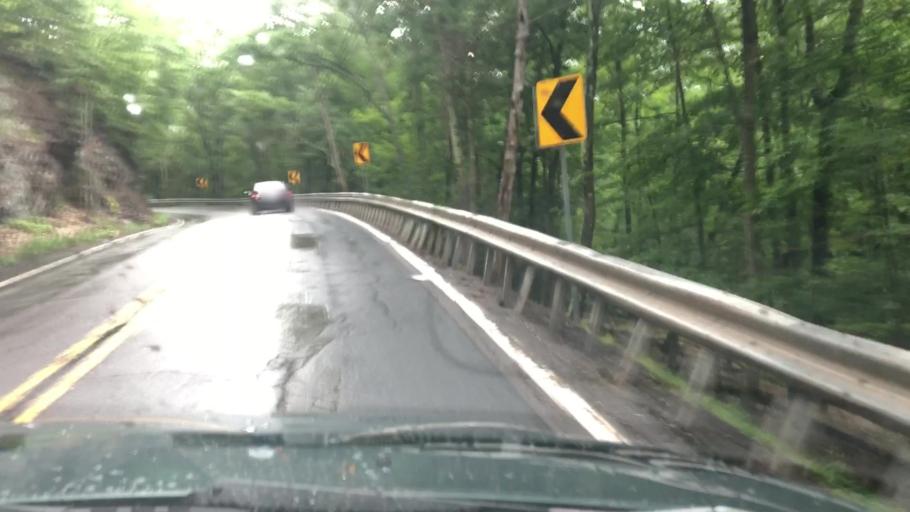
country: US
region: Pennsylvania
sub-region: Monroe County
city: Mountainhome
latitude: 41.2432
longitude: -75.2303
